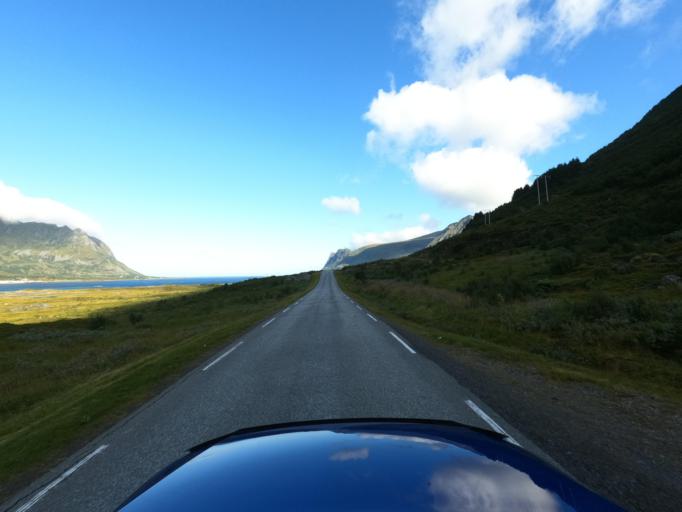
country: NO
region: Nordland
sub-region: Vagan
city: Kabelvag
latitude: 68.2694
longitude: 14.2896
